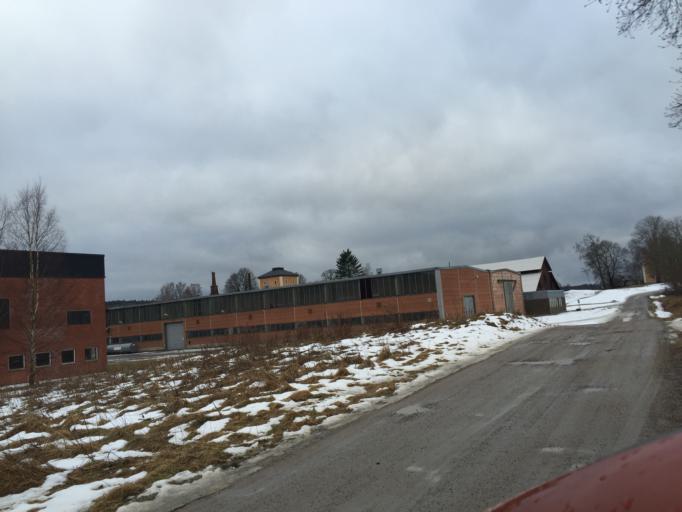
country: SE
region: OErebro
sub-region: Orebro Kommun
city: Odensbacken
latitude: 59.0152
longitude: 15.5822
